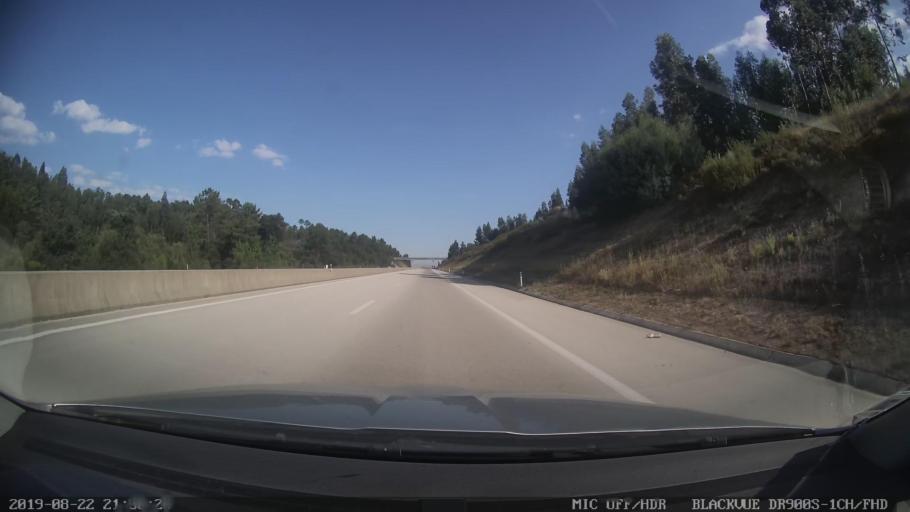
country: PT
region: Coimbra
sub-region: Penela
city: Penela
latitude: 40.0635
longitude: -8.3754
